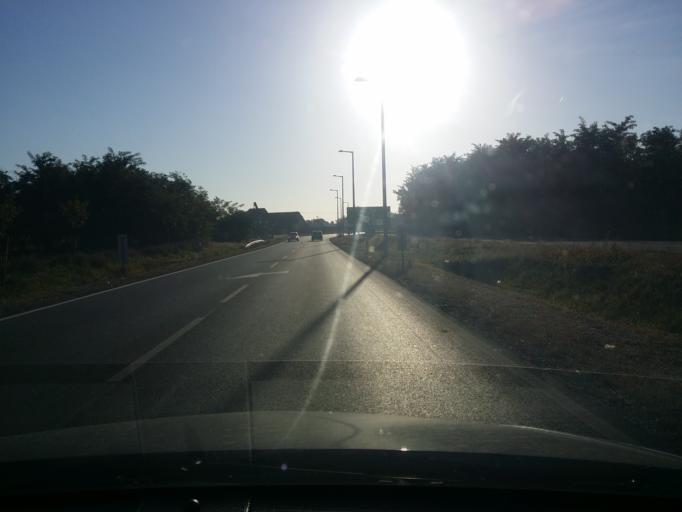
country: HU
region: Bacs-Kiskun
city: Kecskemet
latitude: 46.9062
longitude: 19.7422
